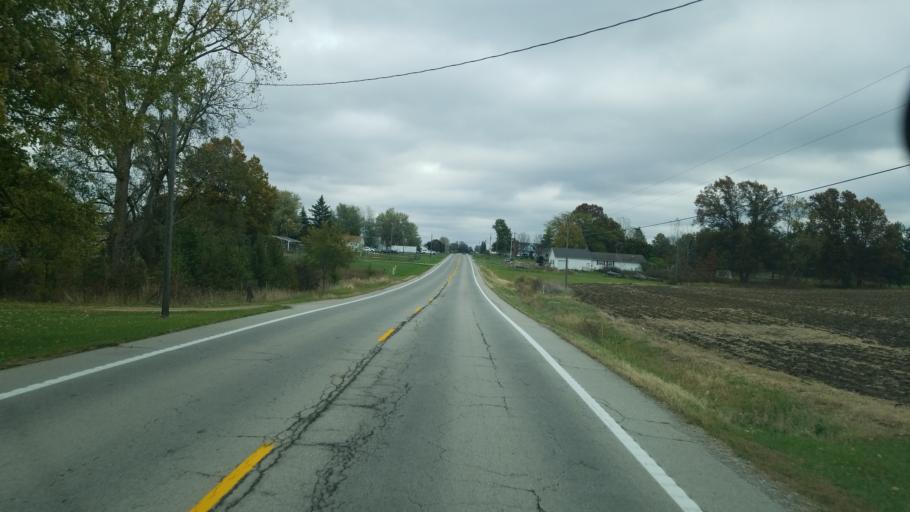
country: US
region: Ohio
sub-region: Huron County
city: Willard
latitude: 41.0435
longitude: -82.7508
